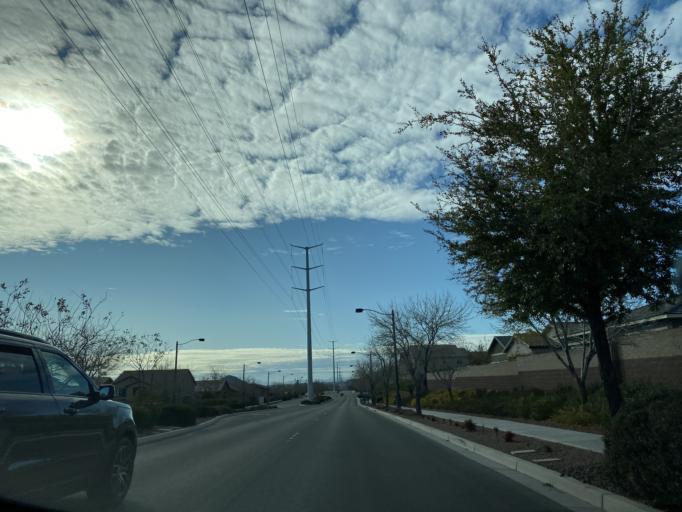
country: US
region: Nevada
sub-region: Clark County
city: Summerlin South
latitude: 36.2909
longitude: -115.3289
